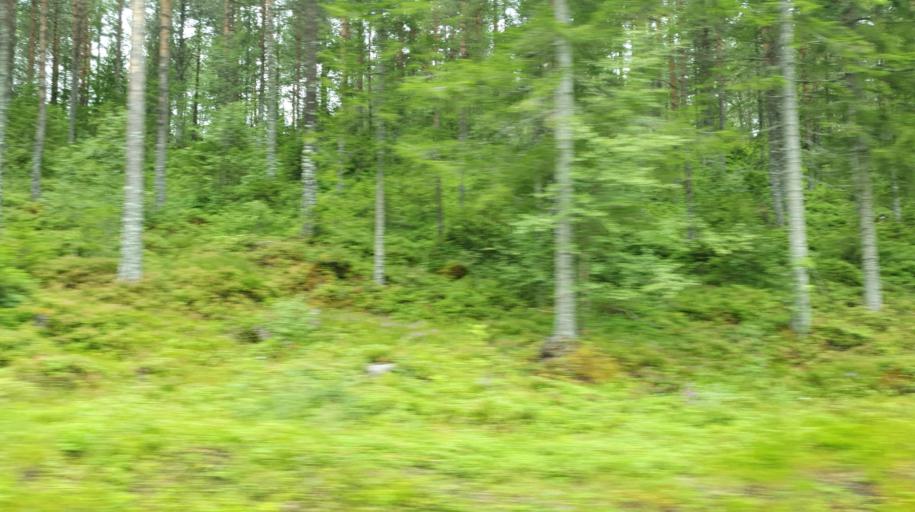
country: NO
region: Nord-Trondelag
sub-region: Stjordal
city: Stjordalshalsen
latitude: 63.4039
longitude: 10.9714
